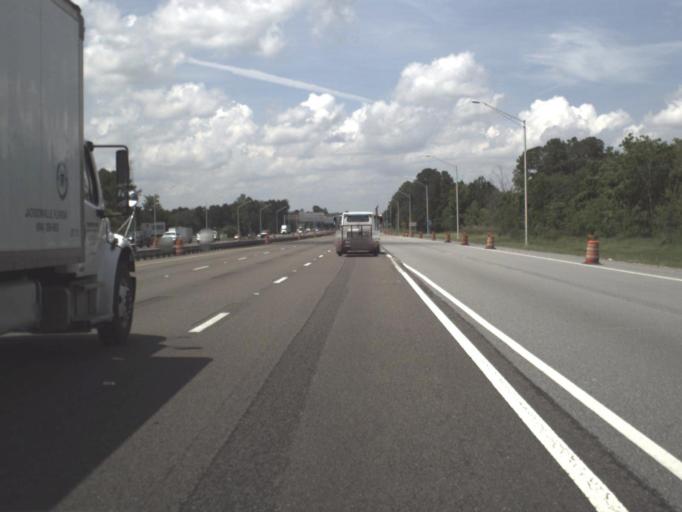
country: US
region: Florida
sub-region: Clay County
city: Bellair-Meadowbrook Terrace
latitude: 30.2125
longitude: -81.7599
